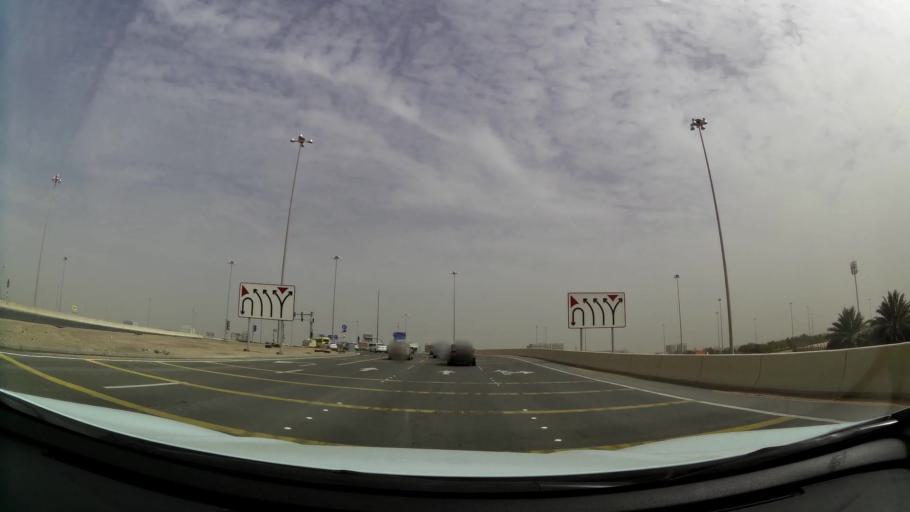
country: AE
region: Abu Dhabi
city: Abu Dhabi
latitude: 24.3241
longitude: 54.5242
